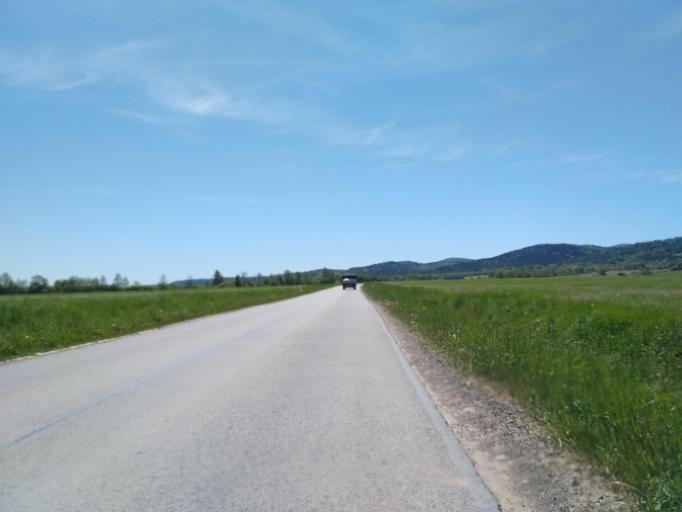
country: PL
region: Subcarpathian Voivodeship
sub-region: Powiat krosnienski
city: Sieniawa
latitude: 49.5360
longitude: 21.9720
